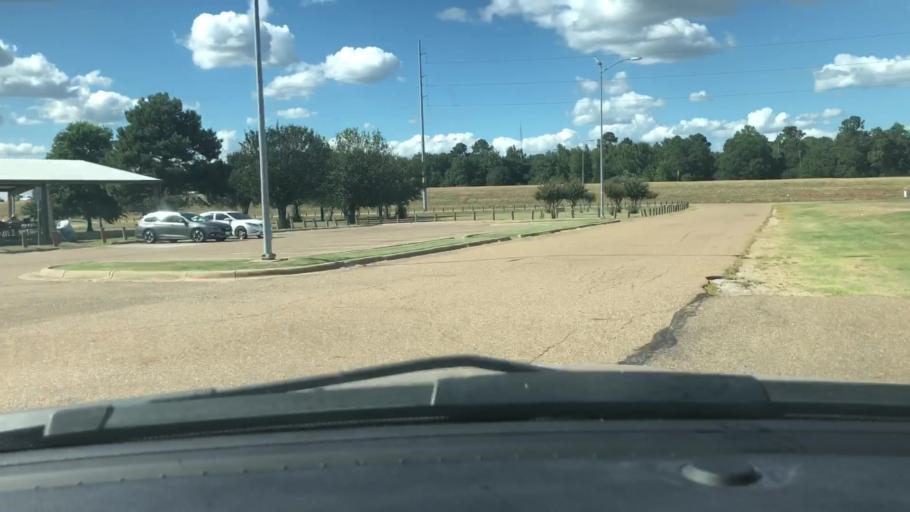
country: US
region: Texas
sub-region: Bowie County
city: Wake Village
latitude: 33.3841
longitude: -94.0881
